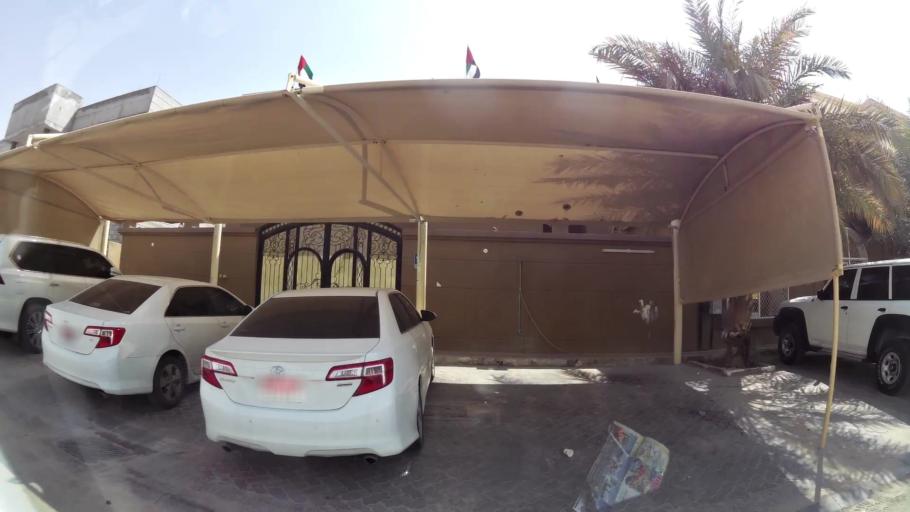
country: AE
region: Abu Dhabi
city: Abu Dhabi
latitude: 24.2995
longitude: 54.6382
